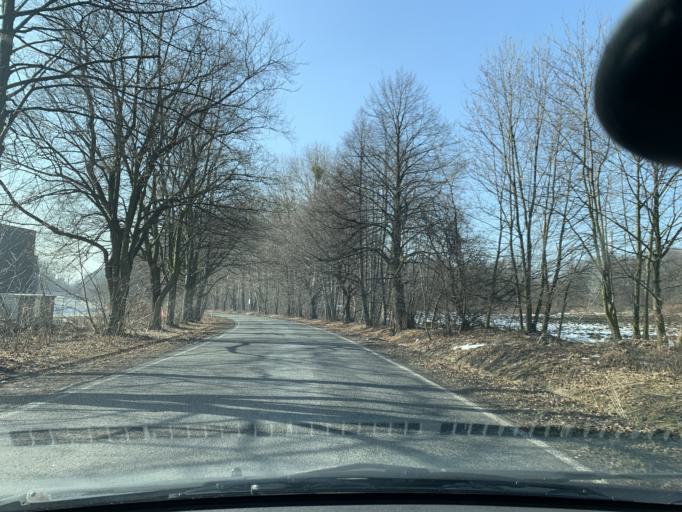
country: PL
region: Silesian Voivodeship
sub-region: Piekary Slaskie
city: Piekary Slaskie
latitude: 50.3790
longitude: 18.9254
